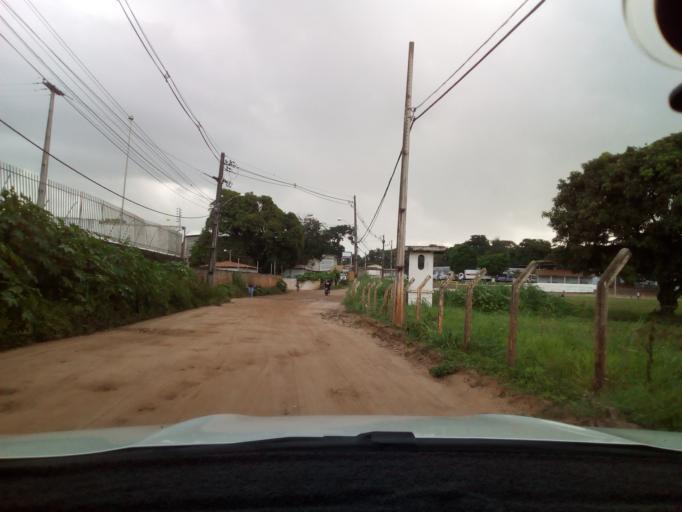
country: BR
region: Paraiba
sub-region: Bayeux
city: Bayeux
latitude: -7.1586
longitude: -34.9073
